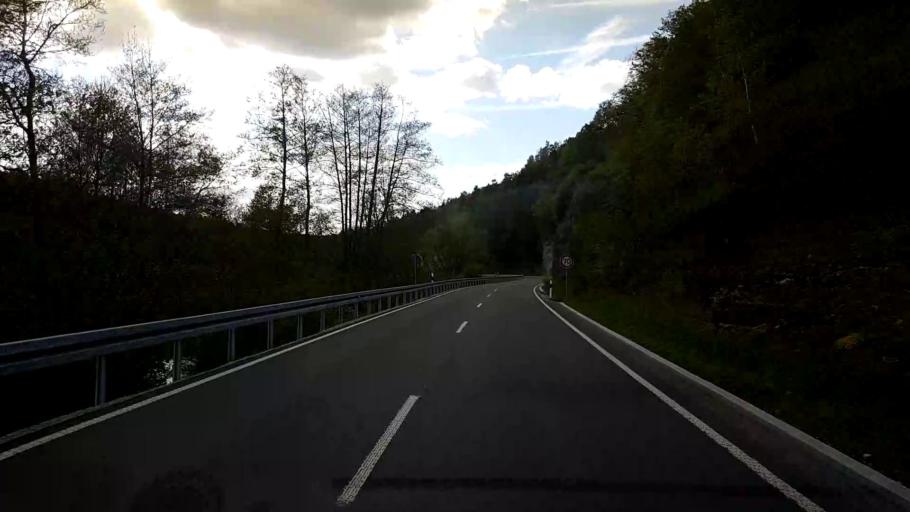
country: DE
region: Bavaria
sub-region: Upper Franconia
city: Hollfeld
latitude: 49.9524
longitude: 11.2738
